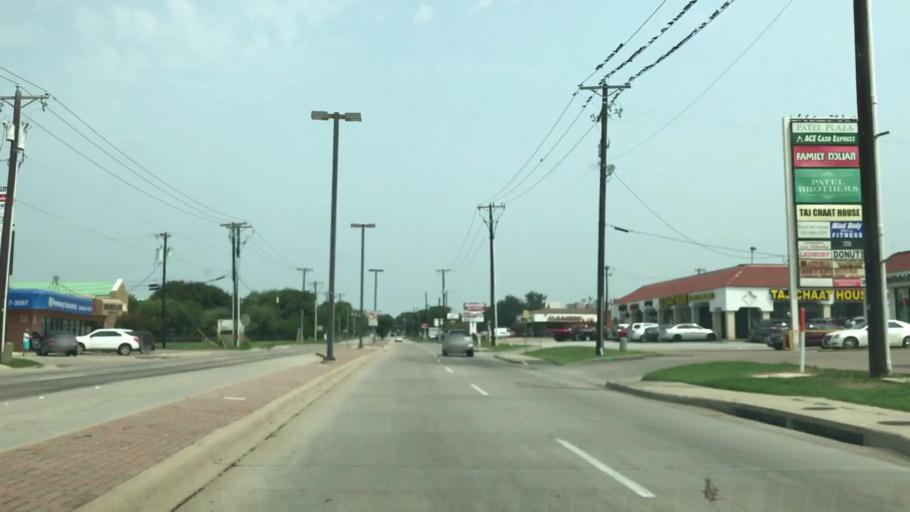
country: US
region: Texas
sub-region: Dallas County
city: Irving
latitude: 32.8444
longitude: -96.9591
